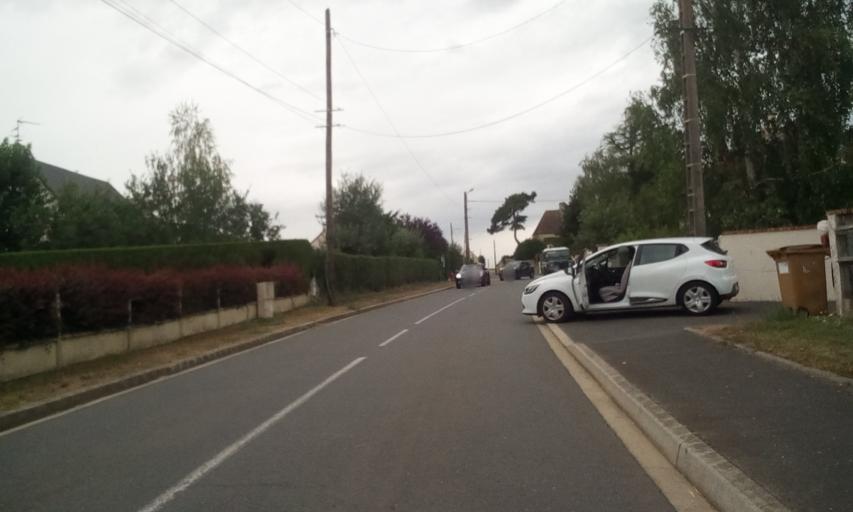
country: FR
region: Lower Normandy
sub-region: Departement du Calvados
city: Bellengreville
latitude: 49.1496
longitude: -0.2252
